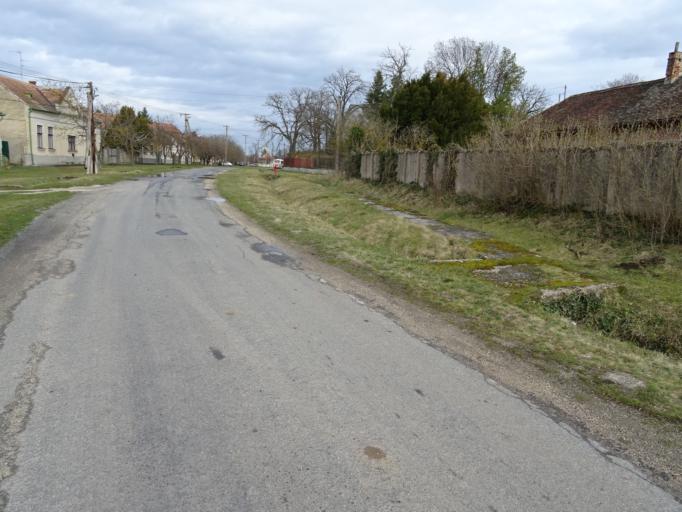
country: HU
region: Gyor-Moson-Sopron
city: Fertoszentmiklos
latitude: 47.4862
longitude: 16.8986
